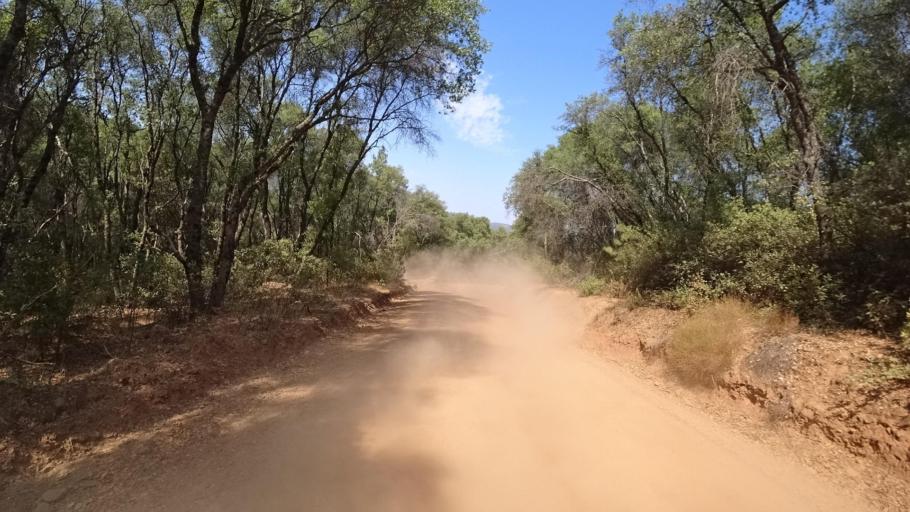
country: US
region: California
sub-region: Mariposa County
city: Midpines
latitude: 37.7001
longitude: -120.1256
